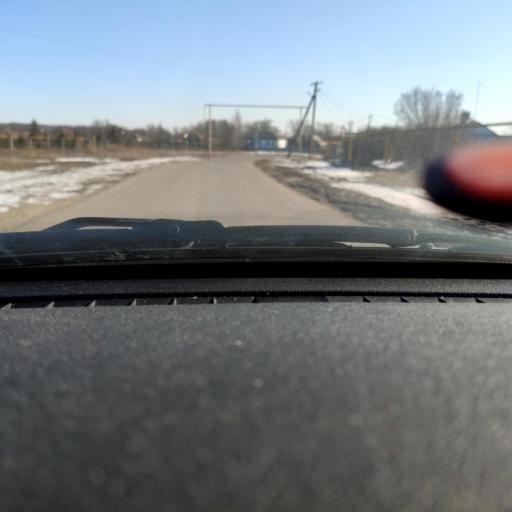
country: RU
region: Voronezj
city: Latnaya
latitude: 51.6981
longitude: 38.9276
